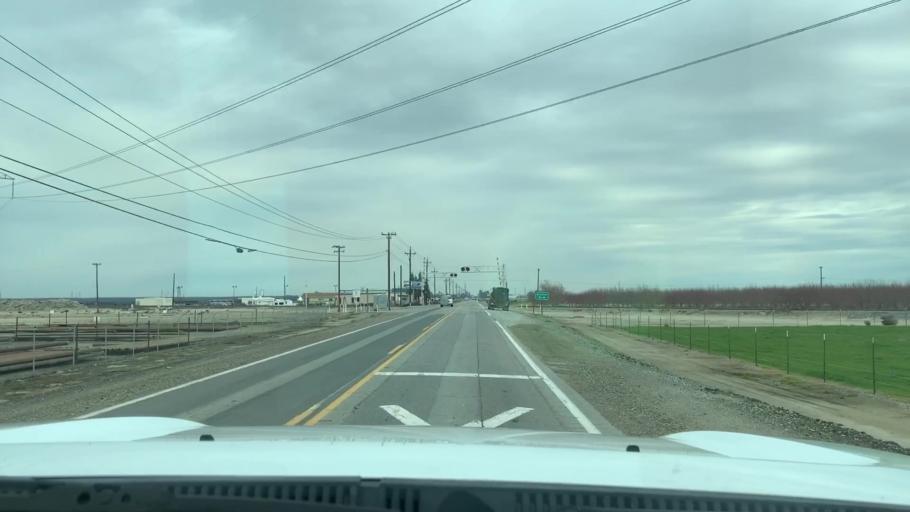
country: US
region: California
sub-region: Kern County
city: Rosedale
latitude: 35.3663
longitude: -119.2521
